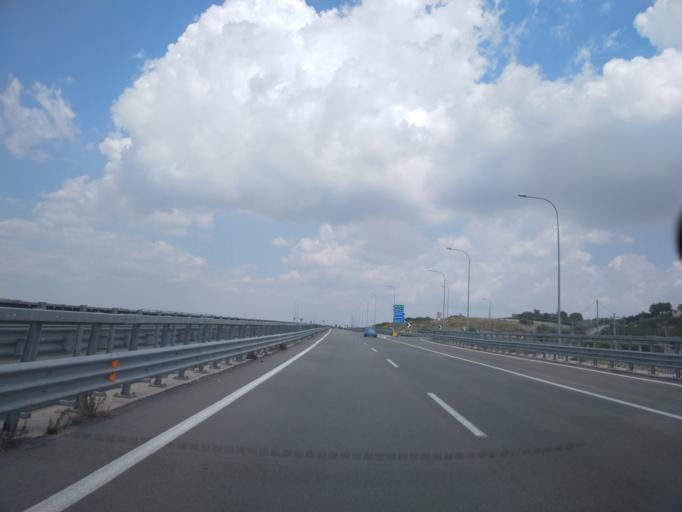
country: IT
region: Sicily
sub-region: Agrigento
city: Canicatti
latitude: 37.3811
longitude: 13.8074
